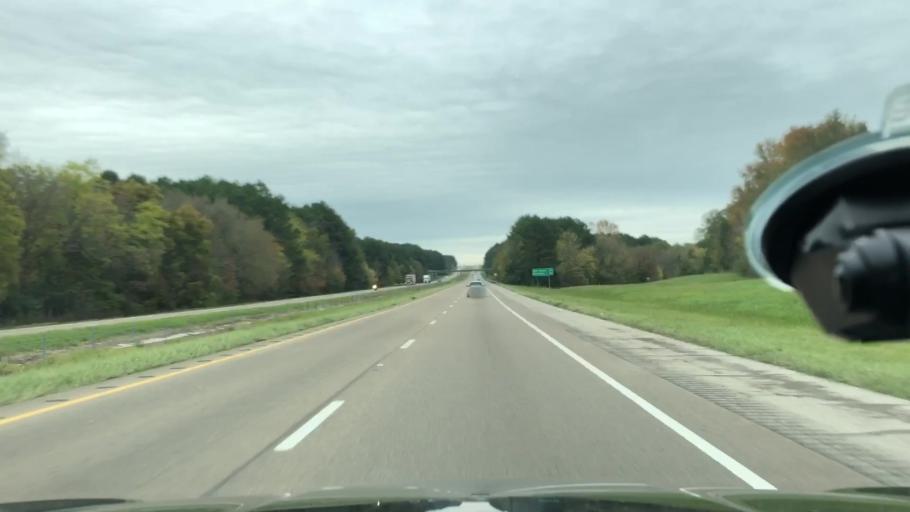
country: US
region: Texas
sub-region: Titus County
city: Mount Pleasant
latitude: 33.1854
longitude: -94.9508
